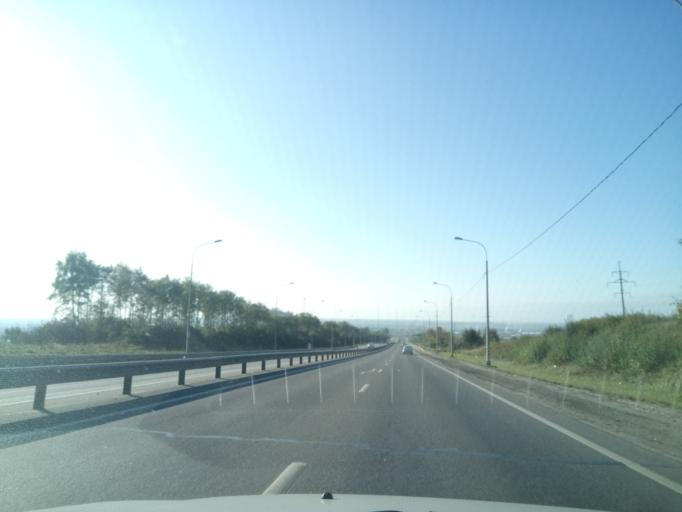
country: RU
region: Nizjnij Novgorod
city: Nizhniy Novgorod
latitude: 56.2029
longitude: 43.9257
